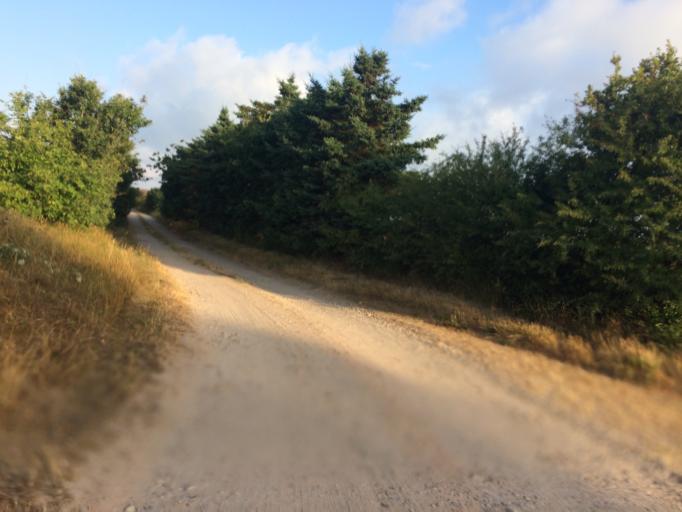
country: DK
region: Central Jutland
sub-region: Struer Kommune
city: Struer
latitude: 56.6073
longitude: 8.6968
